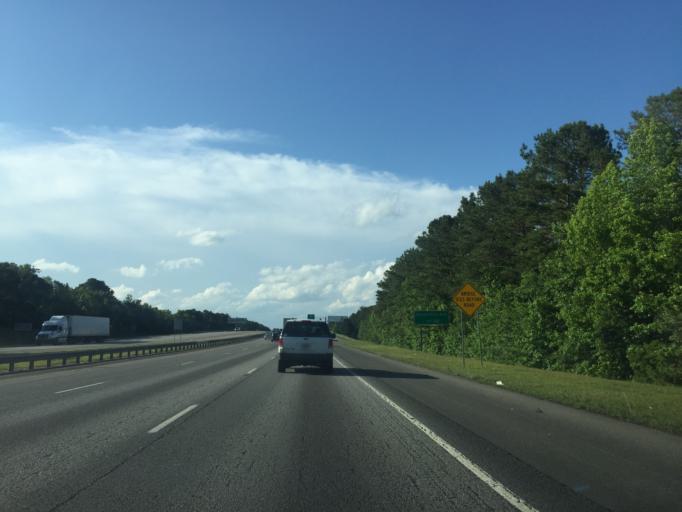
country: US
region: Georgia
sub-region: Chatham County
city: Pooler
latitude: 32.0976
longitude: -81.2364
